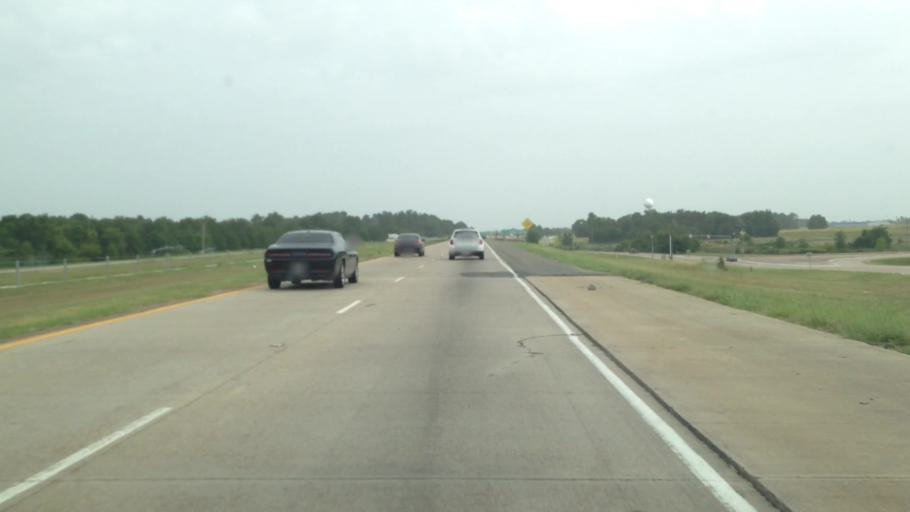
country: US
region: Louisiana
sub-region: Caddo Parish
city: Shreveport
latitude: 32.4396
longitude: -93.8414
